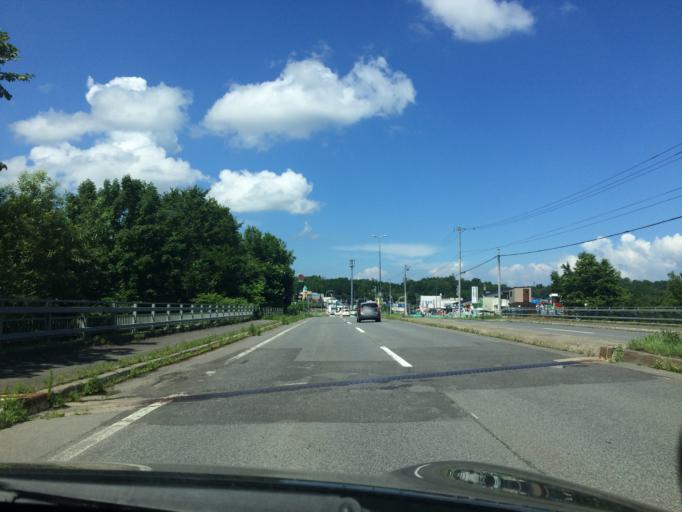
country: JP
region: Hokkaido
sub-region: Asahikawa-shi
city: Asahikawa
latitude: 43.7641
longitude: 142.2805
